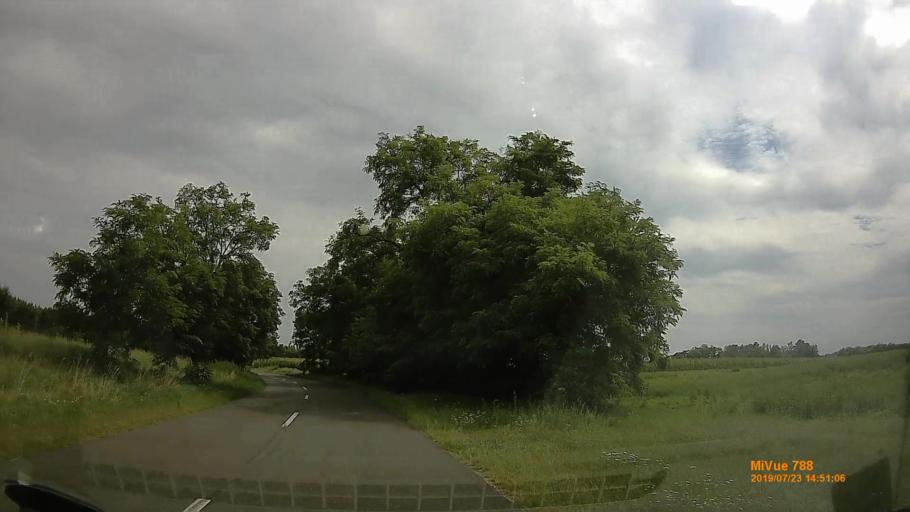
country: HU
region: Szabolcs-Szatmar-Bereg
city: Kalmanhaza
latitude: 47.8854
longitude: 21.6504
